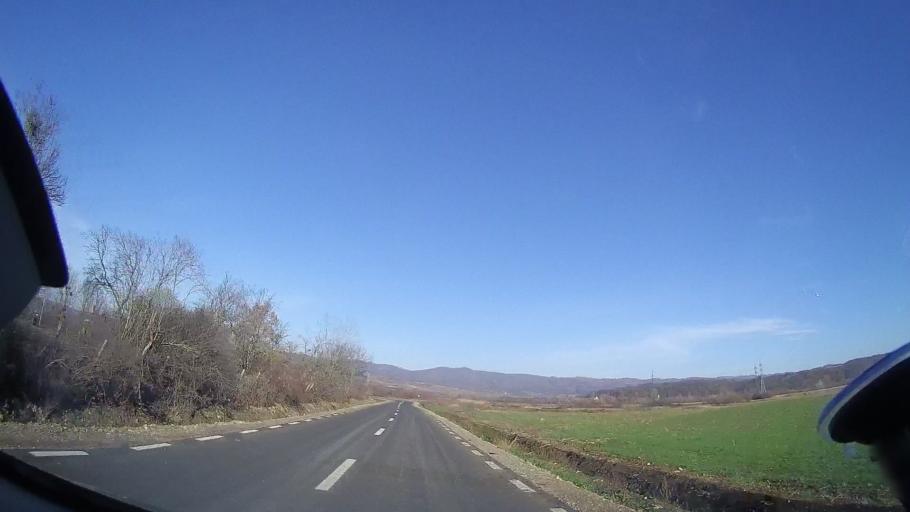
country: RO
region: Bihor
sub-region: Comuna Auseu
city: Auseu
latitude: 47.0069
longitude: 22.5018
